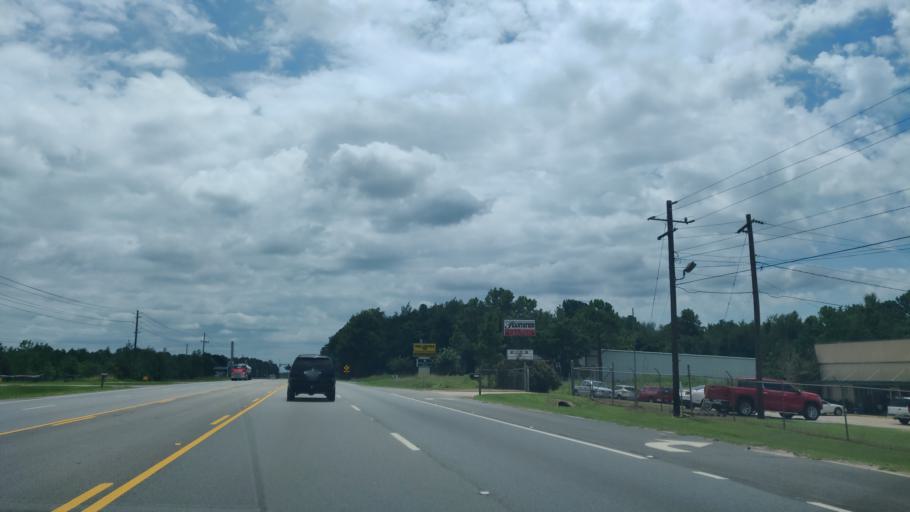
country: US
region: Georgia
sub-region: Dougherty County
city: Albany
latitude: 31.6314
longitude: -84.2412
